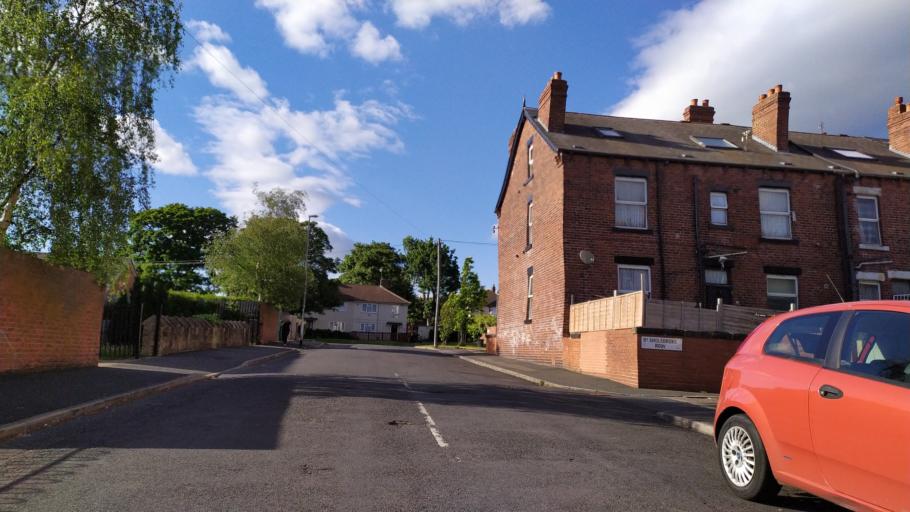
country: GB
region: England
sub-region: City and Borough of Leeds
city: Chapel Allerton
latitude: 53.8193
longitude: -1.5384
